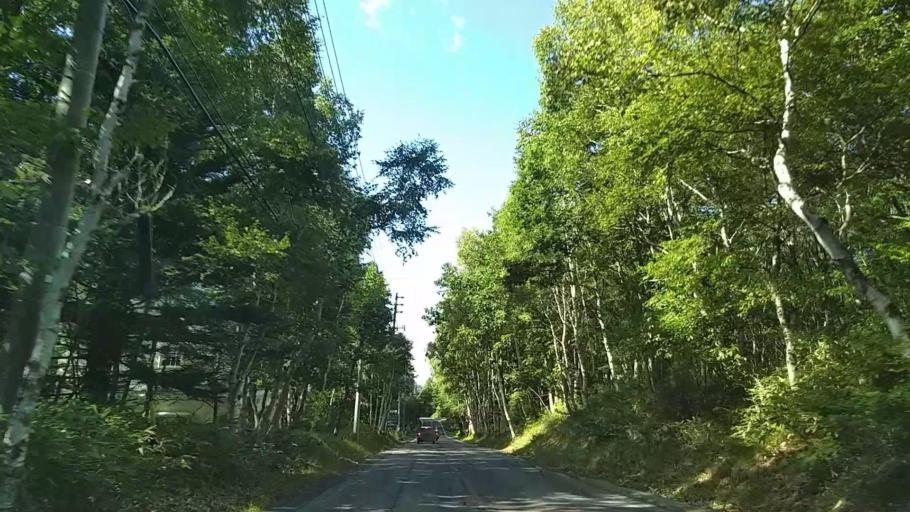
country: JP
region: Nagano
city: Chino
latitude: 36.1033
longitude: 138.2468
